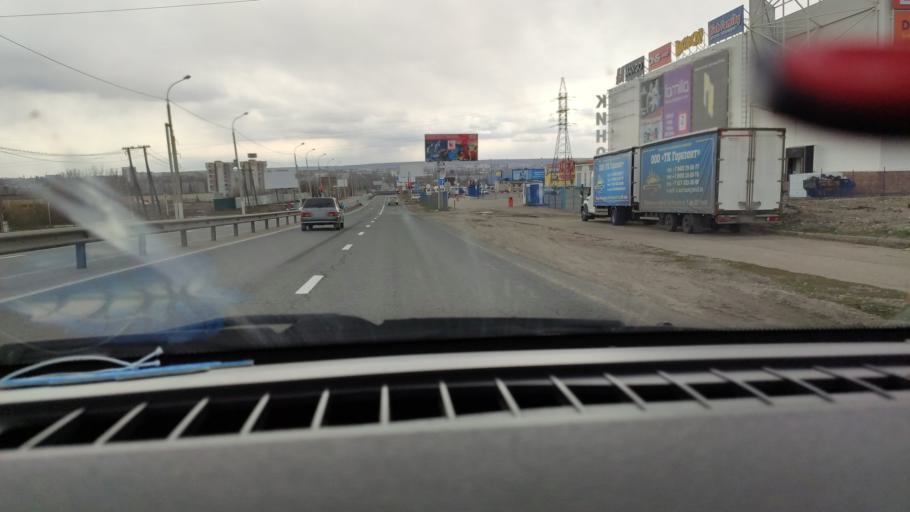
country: RU
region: Saratov
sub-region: Saratovskiy Rayon
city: Saratov
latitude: 51.6220
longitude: 45.9754
